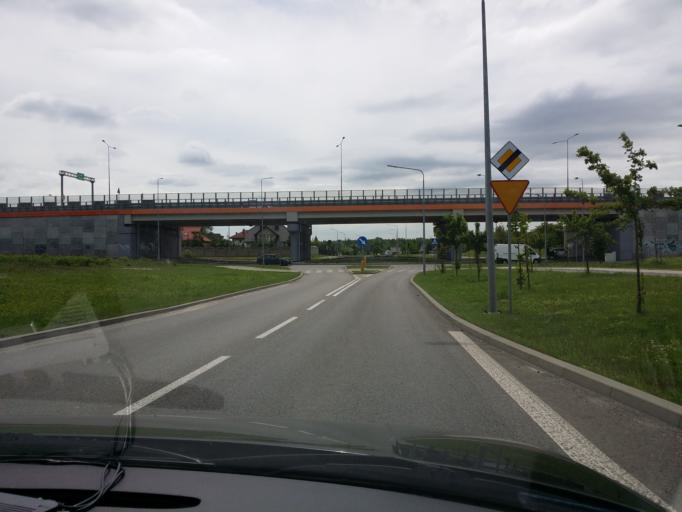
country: PL
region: Masovian Voivodeship
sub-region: Radom
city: Radom
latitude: 51.3719
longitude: 21.1563
